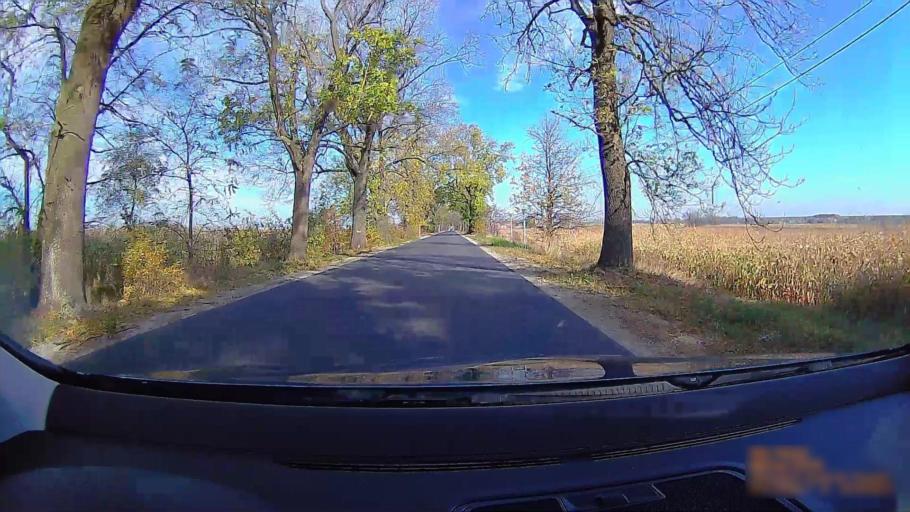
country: PL
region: Greater Poland Voivodeship
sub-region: Powiat ostrzeszowski
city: Doruchow
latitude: 51.3974
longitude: 18.0611
